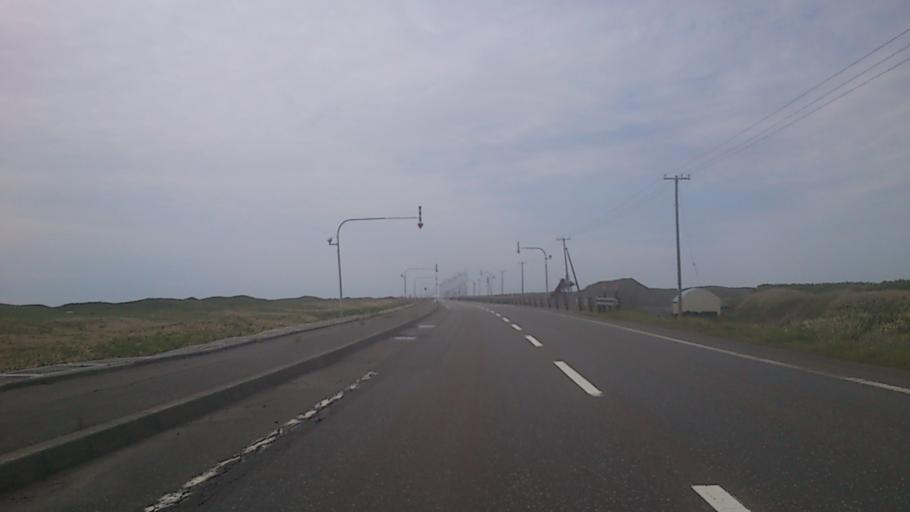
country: JP
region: Hokkaido
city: Makubetsu
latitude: 44.9352
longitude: 141.7181
